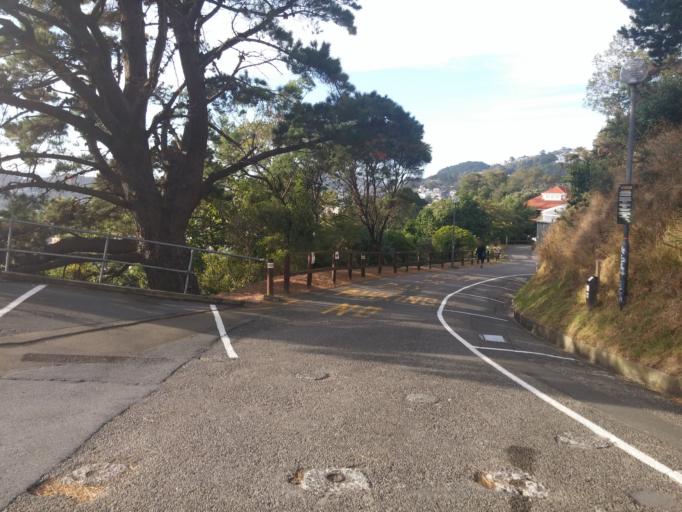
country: NZ
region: Wellington
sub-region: Wellington City
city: Wellington
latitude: -41.2910
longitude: 174.7692
